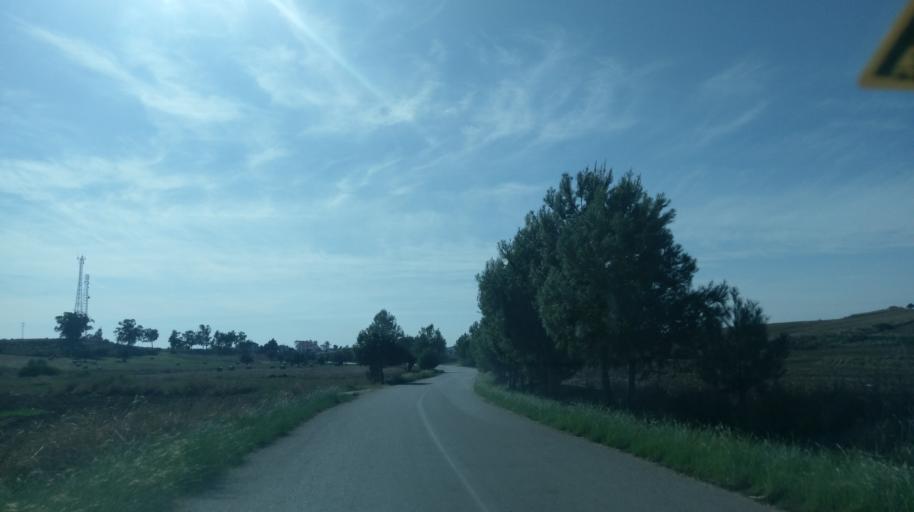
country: CY
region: Ammochostos
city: Trikomo
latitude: 35.3760
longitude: 34.0001
